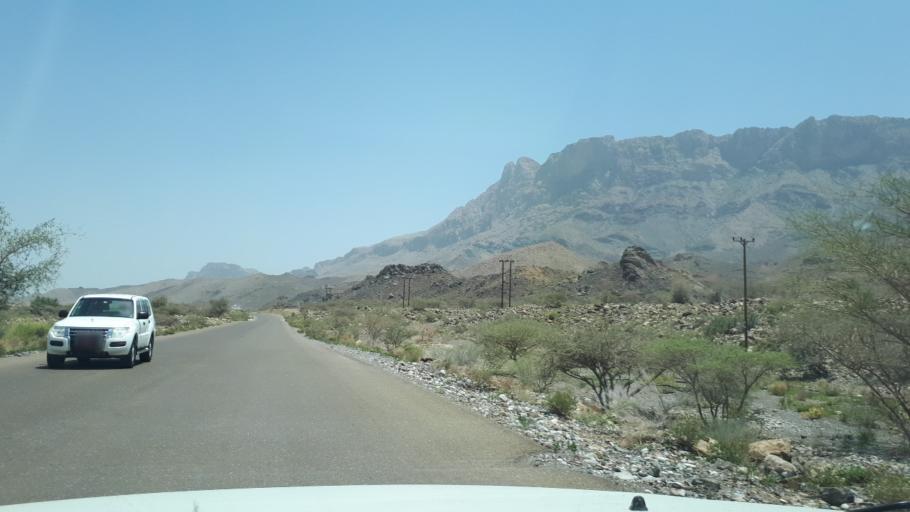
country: OM
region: Muhafazat ad Dakhiliyah
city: Bahla'
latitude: 23.1646
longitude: 57.1616
